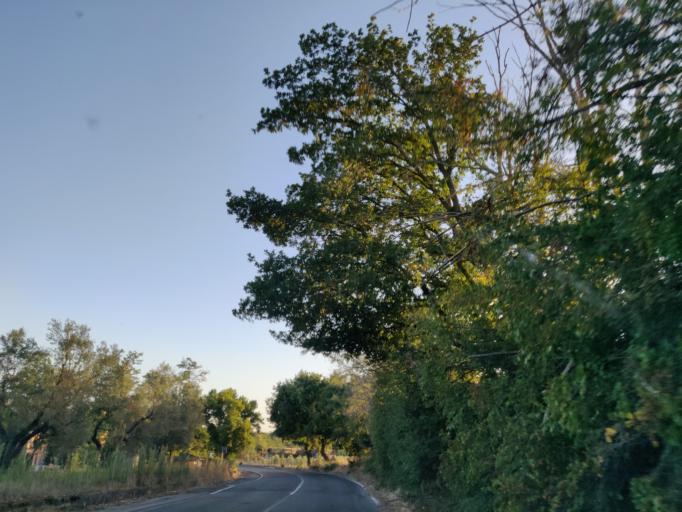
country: IT
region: Latium
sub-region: Provincia di Viterbo
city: Canino
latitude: 42.4140
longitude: 11.7012
